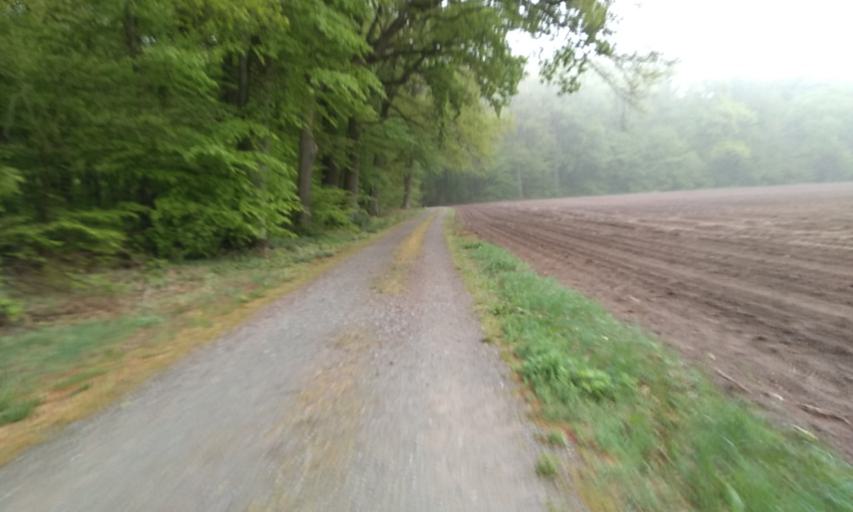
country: DE
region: Lower Saxony
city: Nottensdorf
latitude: 53.4747
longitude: 9.6325
